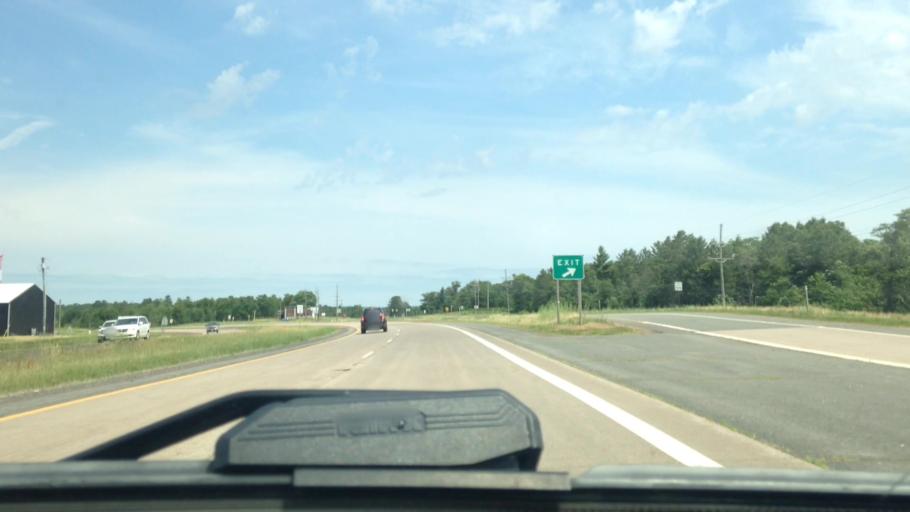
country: US
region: Wisconsin
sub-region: Douglas County
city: Lake Nebagamon
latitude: 46.3172
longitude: -91.8119
